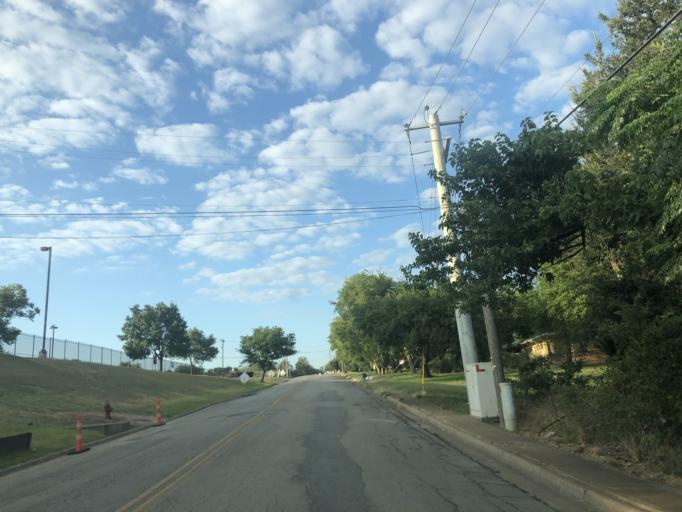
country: US
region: Texas
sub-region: Dallas County
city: Grand Prairie
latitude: 32.7574
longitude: -97.0123
